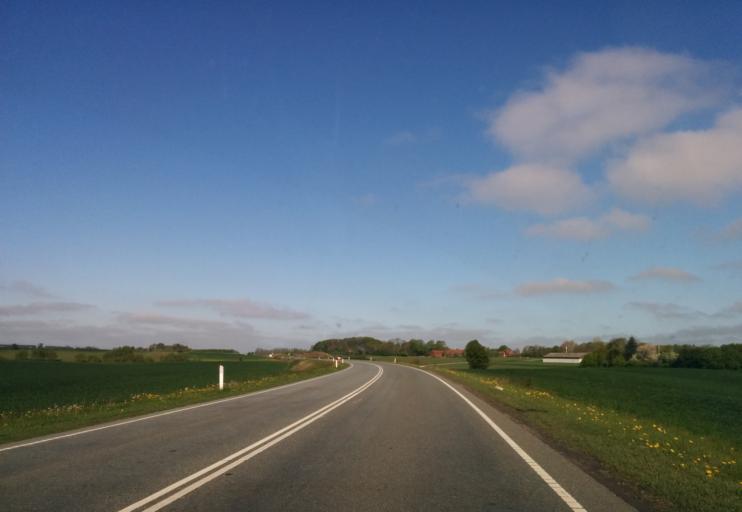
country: DK
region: Central Jutland
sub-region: Arhus Kommune
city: Stavtrup
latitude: 56.1167
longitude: 10.1087
